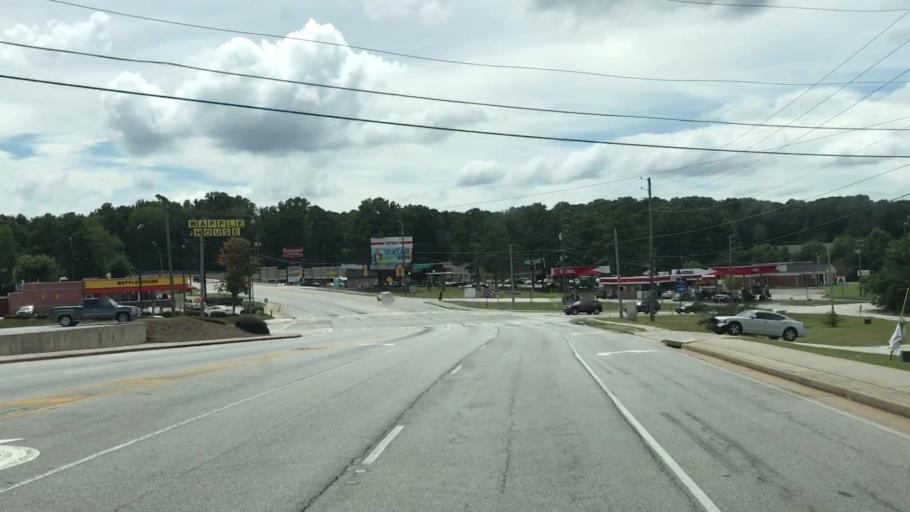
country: US
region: Georgia
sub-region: DeKalb County
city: Lithonia
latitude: 33.7003
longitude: -84.1173
